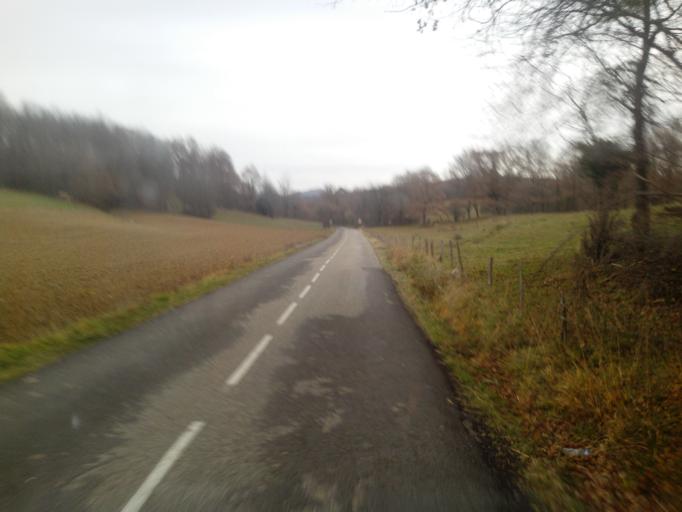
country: FR
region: Midi-Pyrenees
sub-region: Departement de l'Ariege
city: Foix
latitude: 43.0135
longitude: 1.5195
